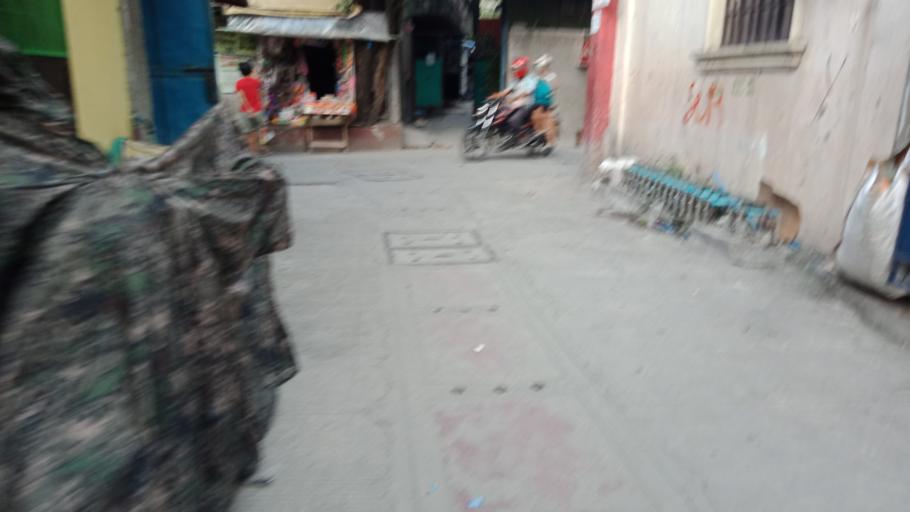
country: PH
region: Calabarzon
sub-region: Province of Rizal
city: Pateros
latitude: 14.5454
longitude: 121.1029
